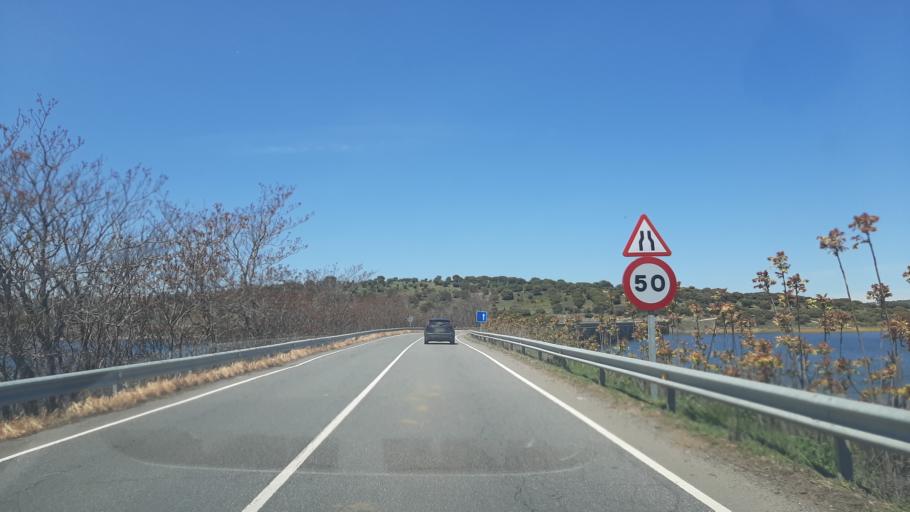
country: ES
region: Castille and Leon
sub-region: Provincia de Salamanca
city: Guijo de Avila
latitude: 40.5510
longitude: -5.6268
